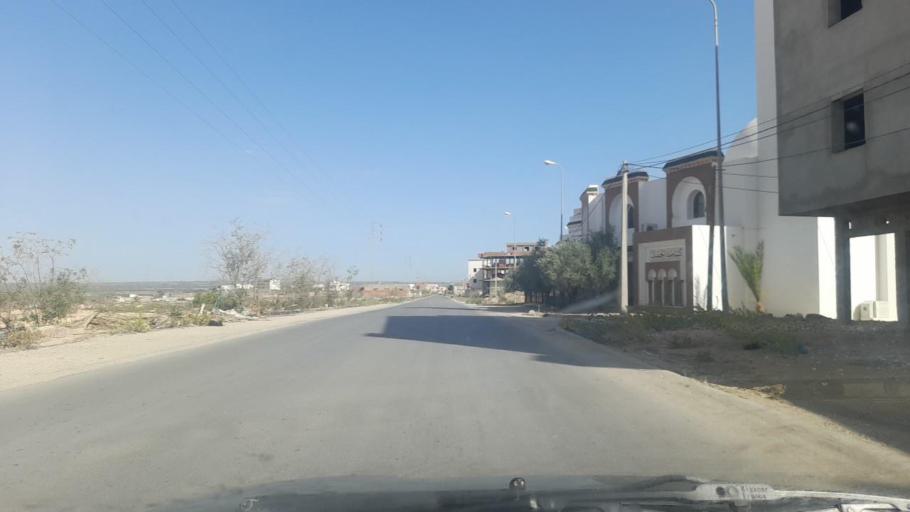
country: TN
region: Susah
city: Akouda
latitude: 35.8129
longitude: 10.5601
